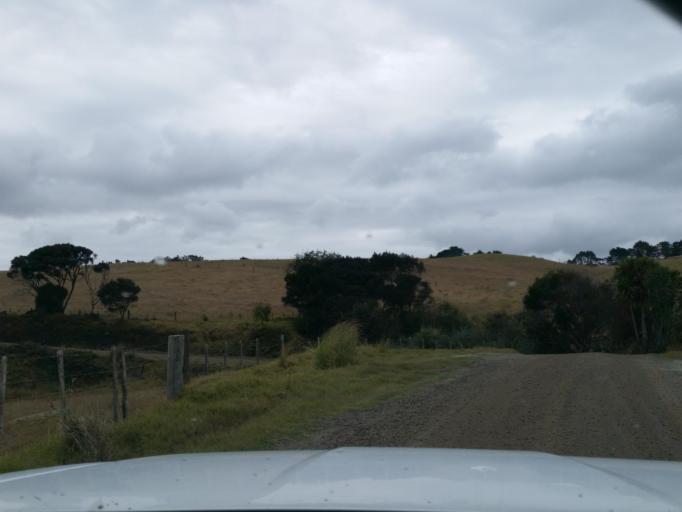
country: NZ
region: Auckland
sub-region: Auckland
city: Wellsford
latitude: -36.2548
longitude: 174.2407
